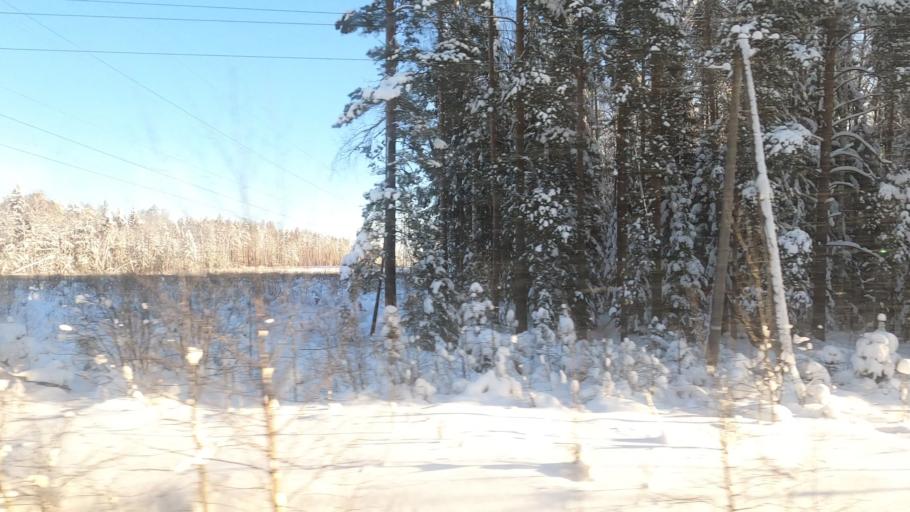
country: RU
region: Moskovskaya
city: Zhukovka
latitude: 56.4830
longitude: 37.5490
